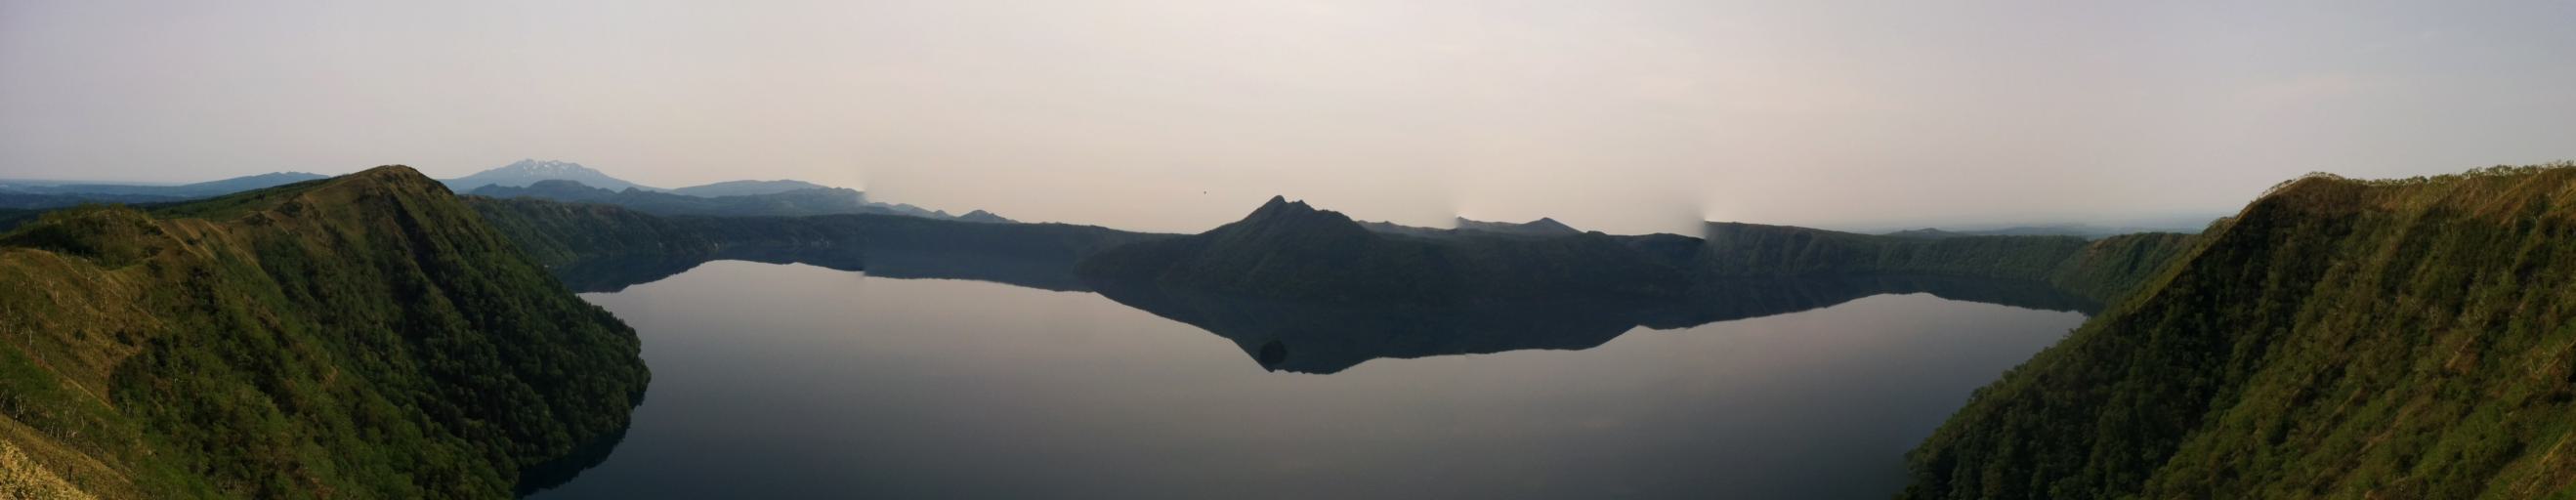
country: JP
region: Hokkaido
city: Bihoro
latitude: 43.5829
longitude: 144.5024
